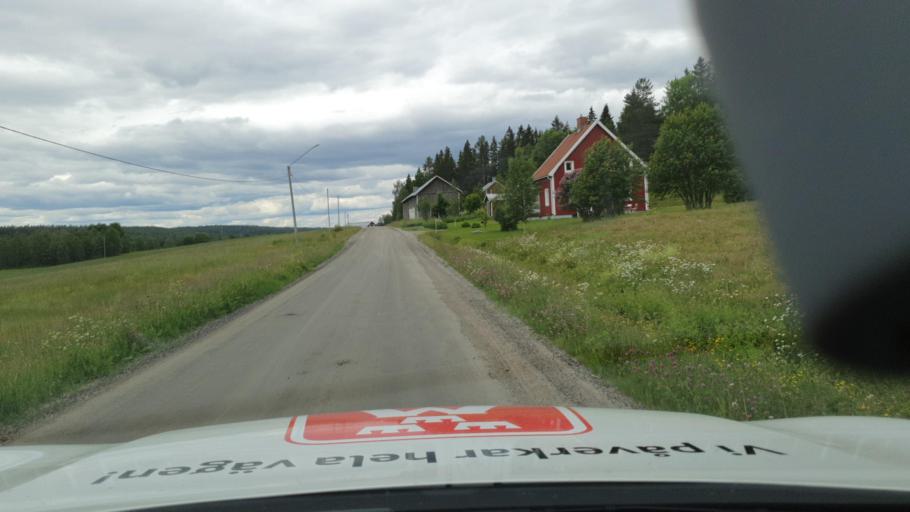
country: SE
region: Vaesterbotten
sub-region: Nordmalings Kommun
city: Nordmaling
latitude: 63.7179
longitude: 19.3277
